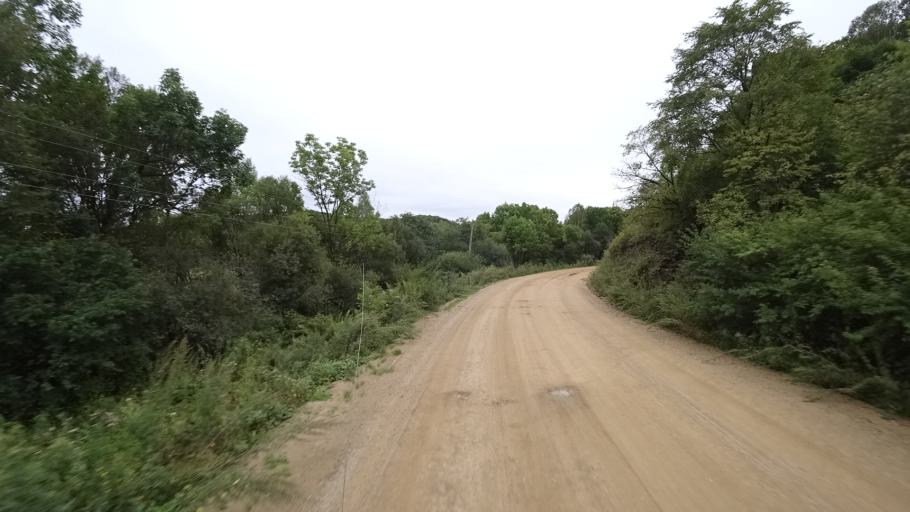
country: RU
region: Primorskiy
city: Rettikhovka
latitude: 44.1797
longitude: 132.8667
